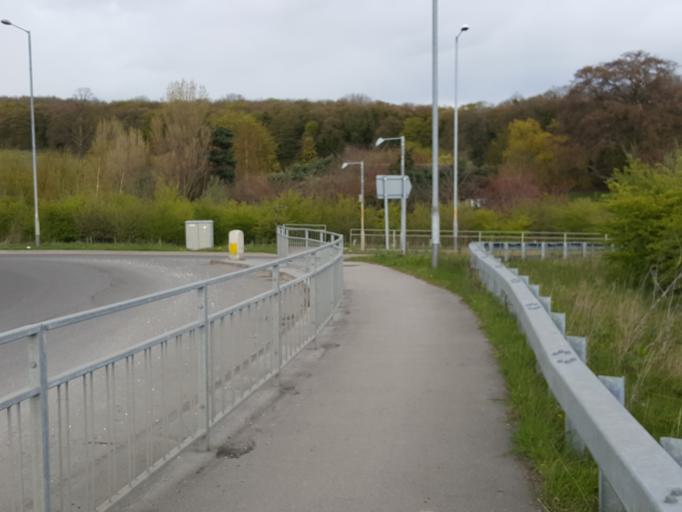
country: GB
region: England
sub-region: East Riding of Yorkshire
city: North Ferriby
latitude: 53.7245
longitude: -0.5198
